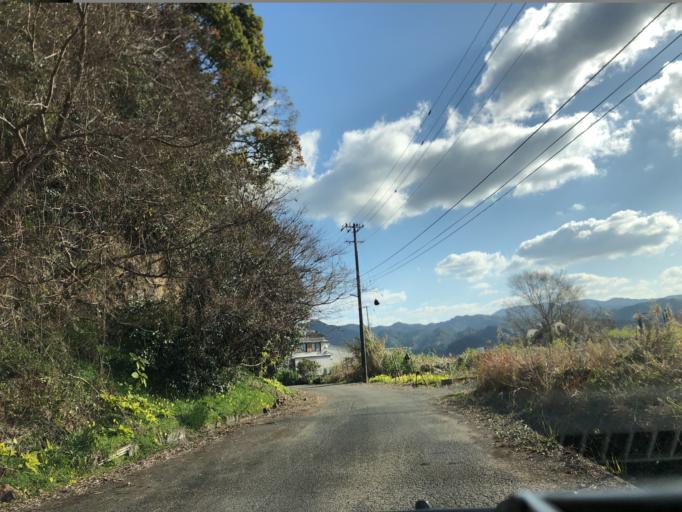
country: JP
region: Kochi
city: Sukumo
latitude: 32.9122
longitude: 132.7001
